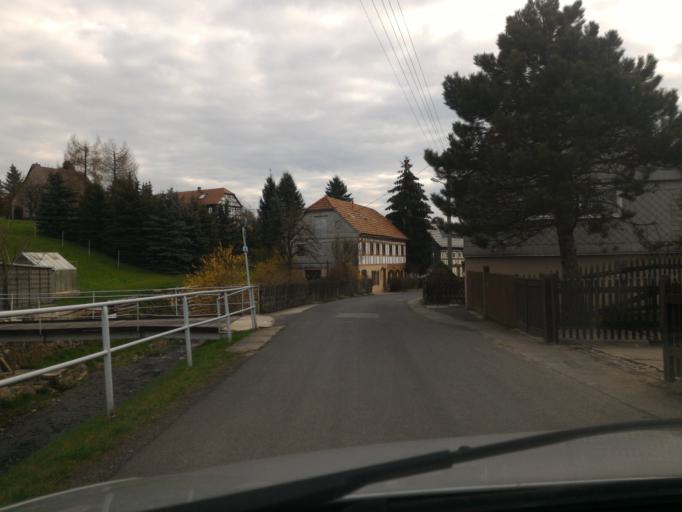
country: DE
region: Saxony
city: Eibau
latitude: 50.9751
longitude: 14.6849
